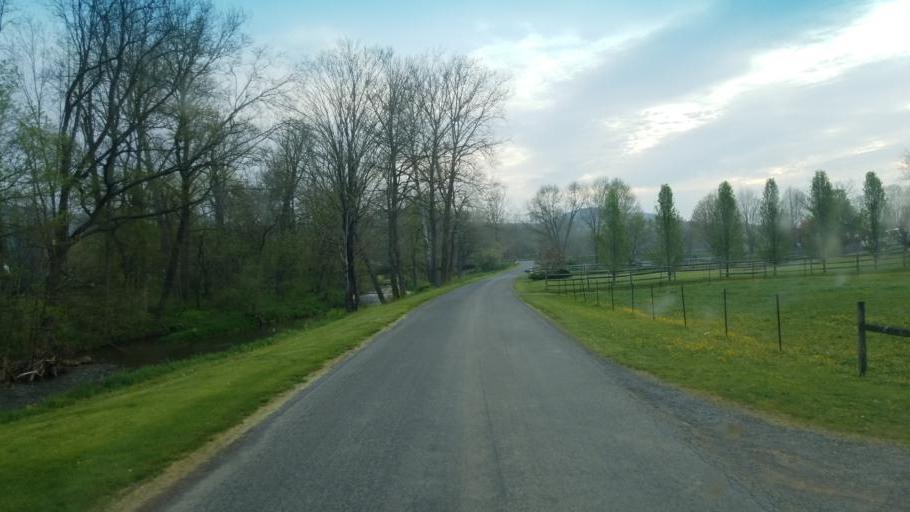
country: US
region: Virginia
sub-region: Smyth County
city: Marion
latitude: 36.7713
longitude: -81.4533
